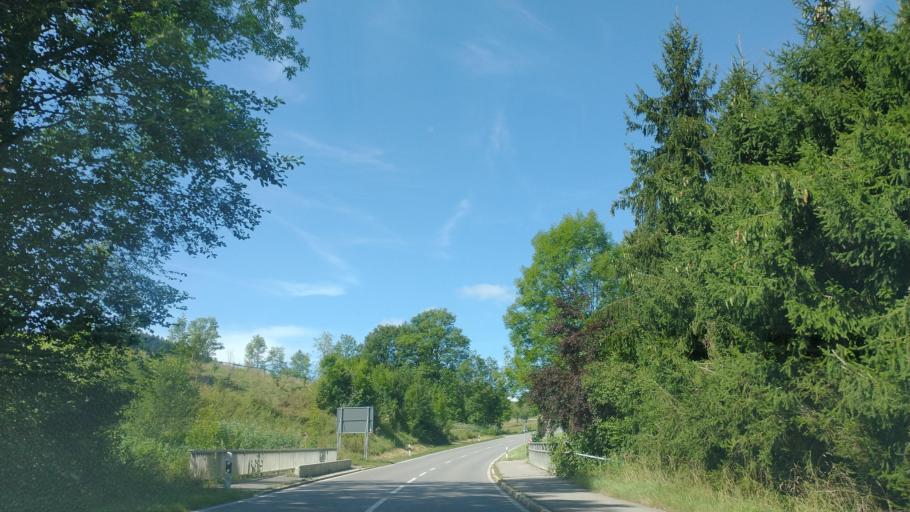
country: DE
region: Baden-Wuerttemberg
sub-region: Tuebingen Region
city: Neukirch
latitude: 47.6684
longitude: 9.7332
